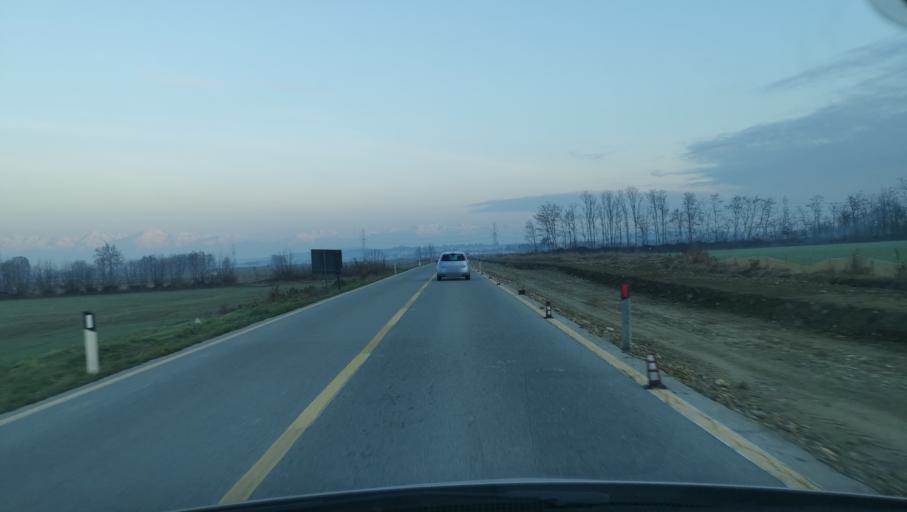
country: IT
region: Piedmont
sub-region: Provincia di Torino
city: Caluso
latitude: 45.2681
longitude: 7.8923
